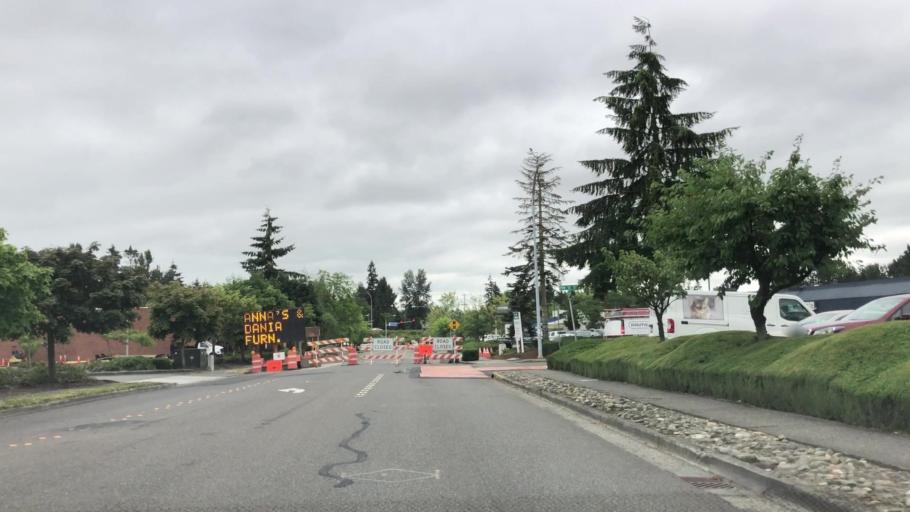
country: US
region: Washington
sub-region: Snohomish County
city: Alderwood Manor
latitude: 47.8198
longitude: -122.2871
